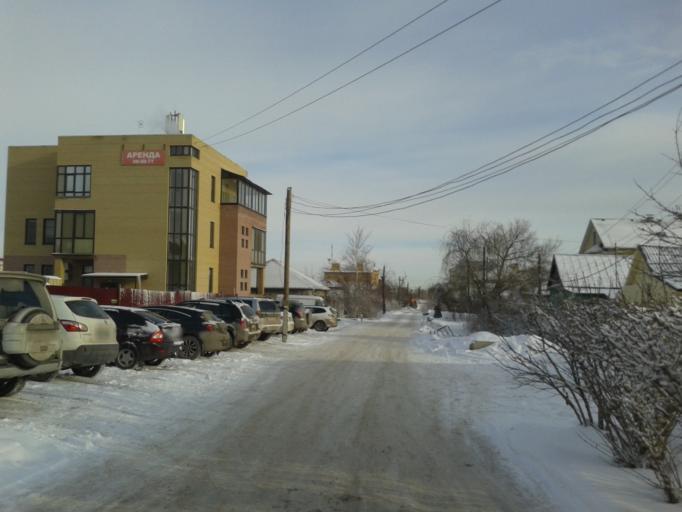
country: RU
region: Volgograd
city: Volgograd
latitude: 48.7238
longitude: 44.5096
